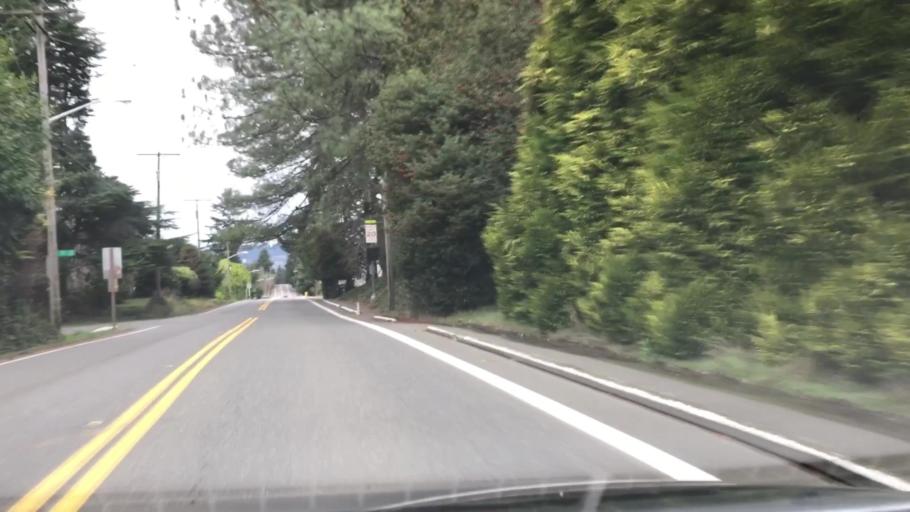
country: US
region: Washington
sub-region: King County
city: East Hill-Meridian
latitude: 47.4087
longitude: -122.1998
